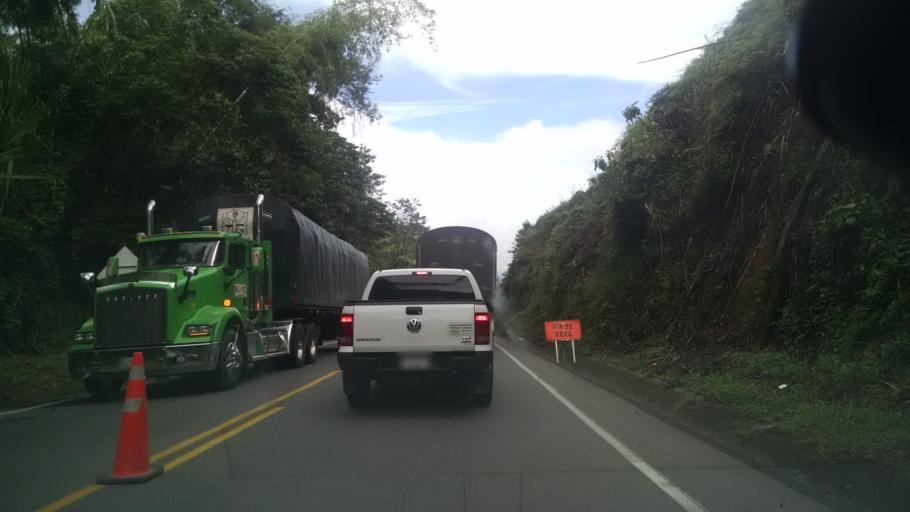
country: CO
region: Caldas
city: Palestina
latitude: 5.0756
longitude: -75.6465
